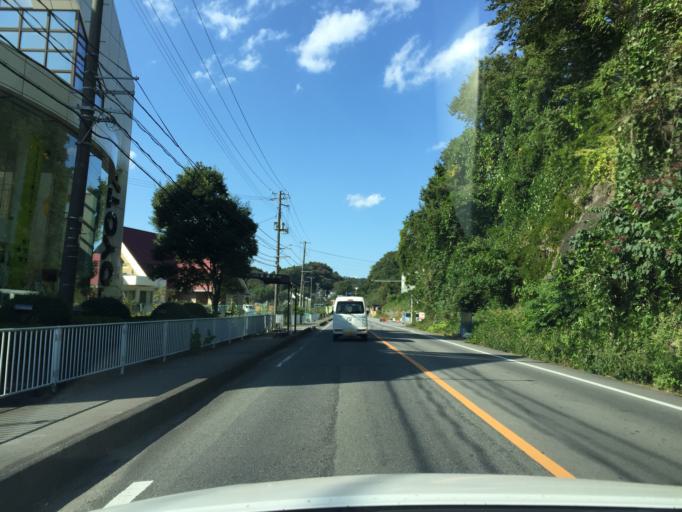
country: JP
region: Fukushima
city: Iwaki
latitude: 37.0203
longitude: 140.9013
